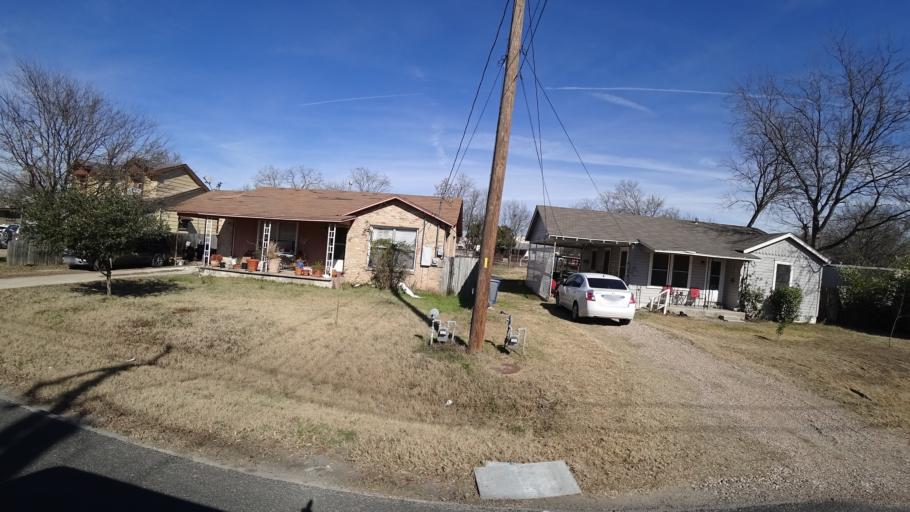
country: US
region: Texas
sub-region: Travis County
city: Wells Branch
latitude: 30.3759
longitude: -97.6874
